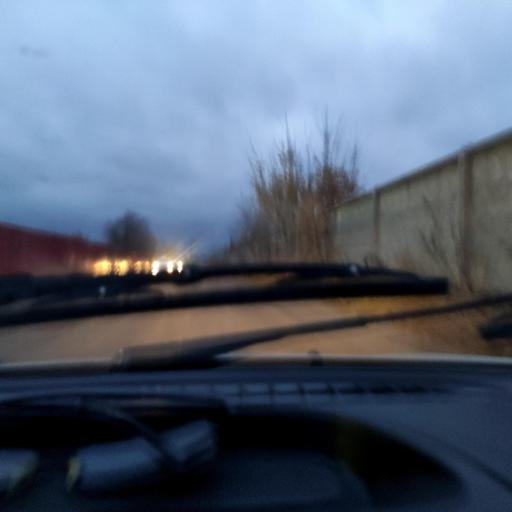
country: RU
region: Samara
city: Tol'yatti
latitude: 53.5667
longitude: 49.4834
